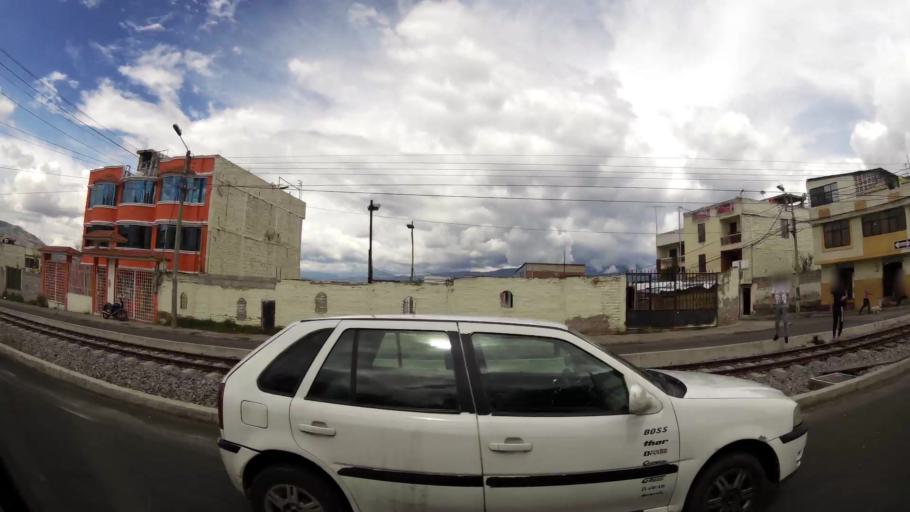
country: EC
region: Tungurahua
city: Ambato
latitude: -1.2522
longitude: -78.6189
